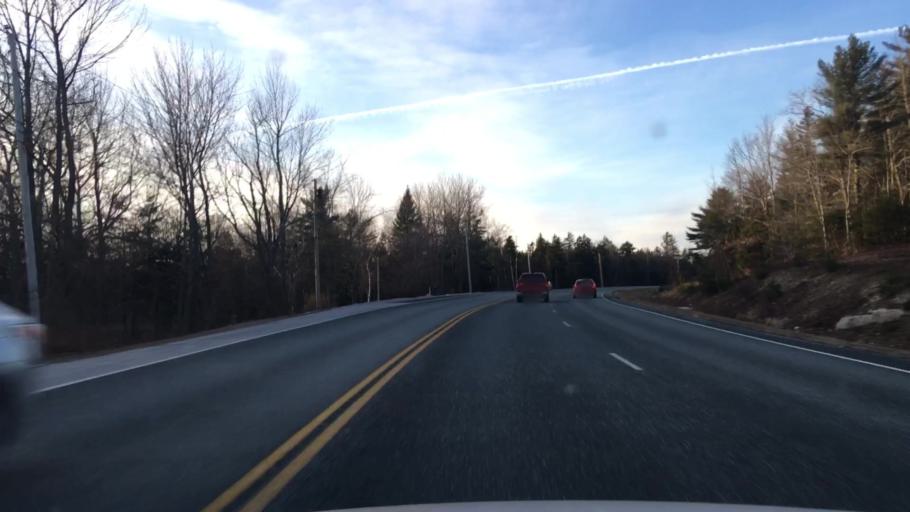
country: US
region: Maine
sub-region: Hancock County
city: Dedham
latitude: 44.6456
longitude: -68.5597
